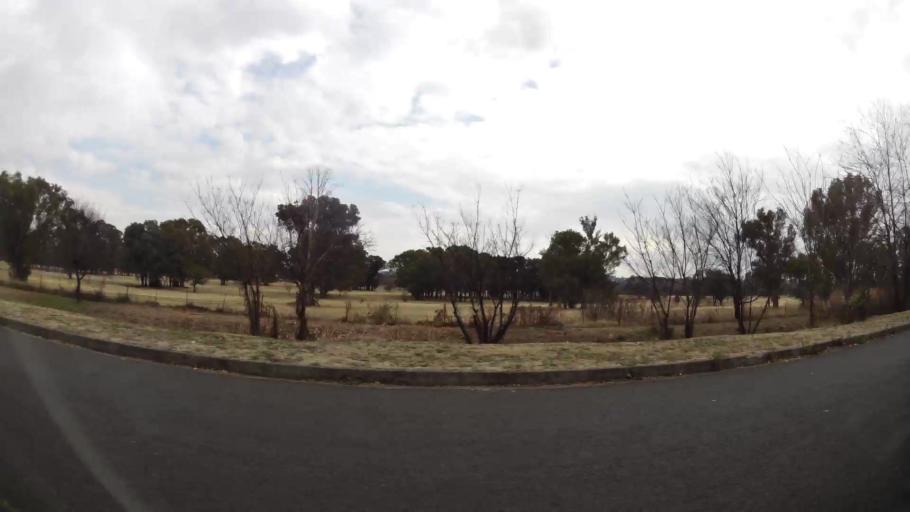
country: ZA
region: Orange Free State
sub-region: Fezile Dabi District Municipality
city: Kroonstad
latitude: -27.6706
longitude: 27.2457
